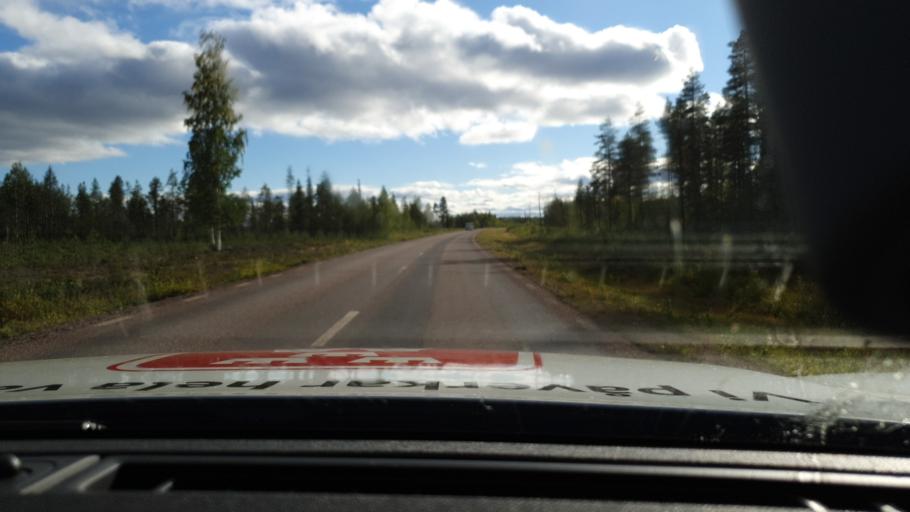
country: SE
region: Norrbotten
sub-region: Pajala Kommun
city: Pajala
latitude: 67.1065
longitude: 22.5972
